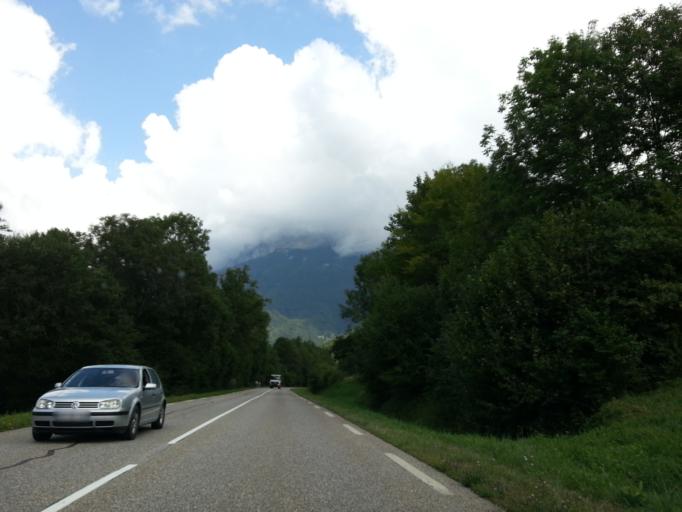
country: FR
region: Rhone-Alpes
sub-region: Departement de la Haute-Savoie
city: Dingy-Saint-Clair
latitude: 45.8811
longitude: 6.2205
